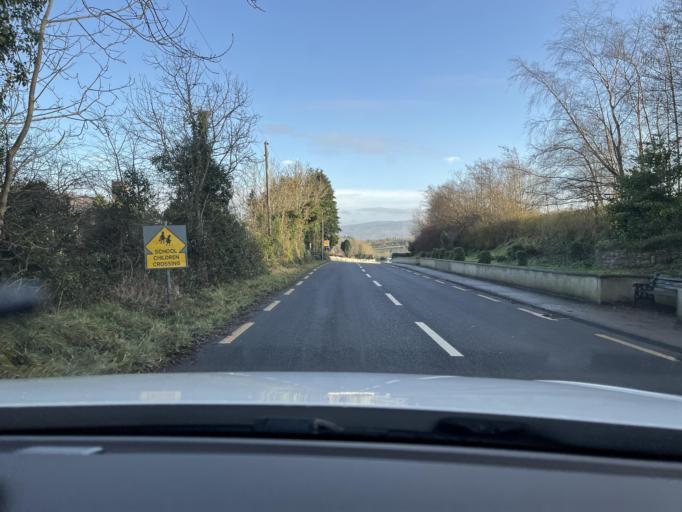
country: IE
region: Connaught
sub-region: County Leitrim
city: Manorhamilton
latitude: 54.1692
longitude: -8.1411
